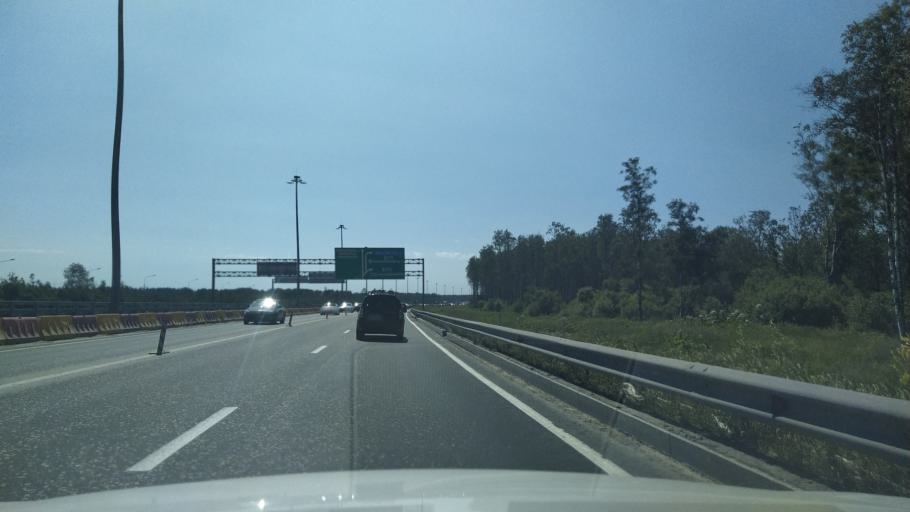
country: RU
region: St.-Petersburg
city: Levashovo
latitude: 60.0670
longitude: 30.1691
